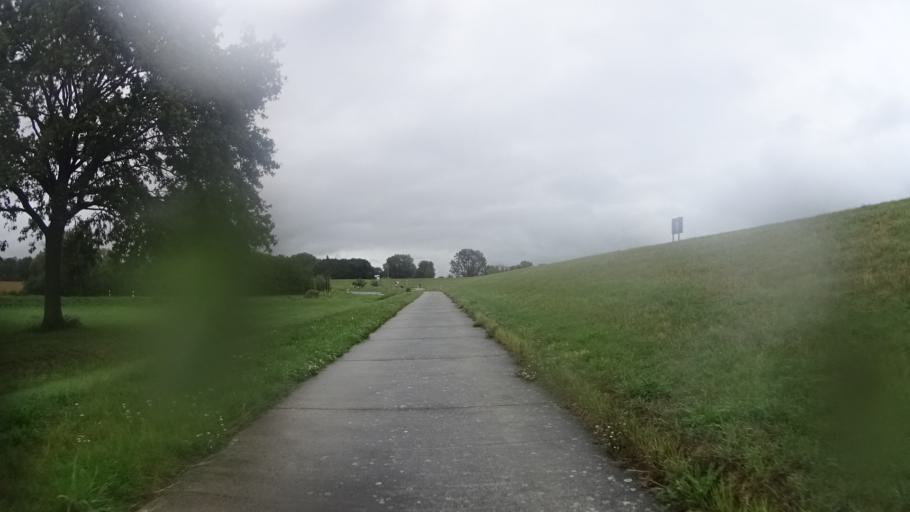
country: DE
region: Lower Saxony
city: Damnatz
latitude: 53.1658
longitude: 11.1259
